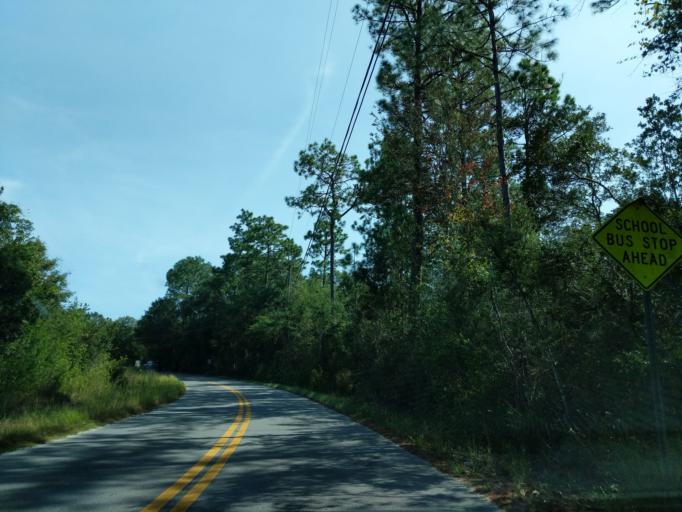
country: US
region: Florida
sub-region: Okaloosa County
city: Crestview
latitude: 30.7064
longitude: -86.5957
